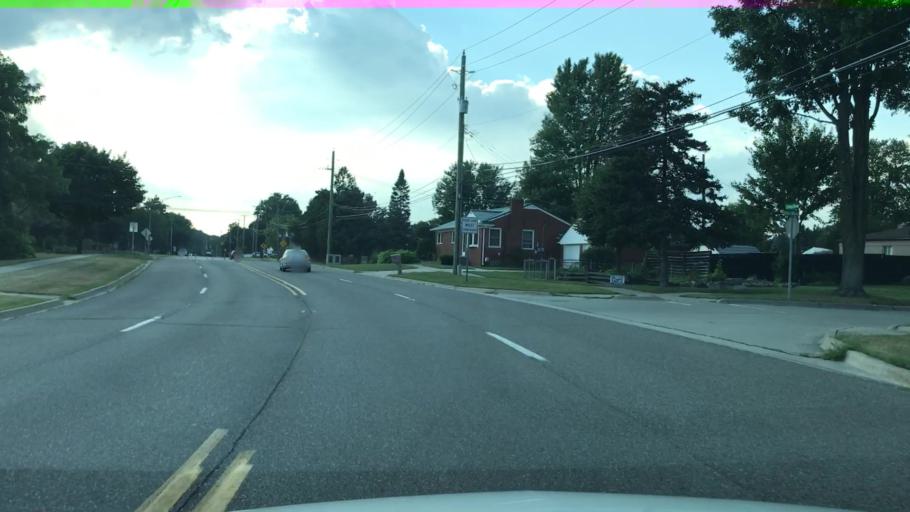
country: US
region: Michigan
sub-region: Macomb County
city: Sterling Heights
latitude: 42.6003
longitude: -83.0058
